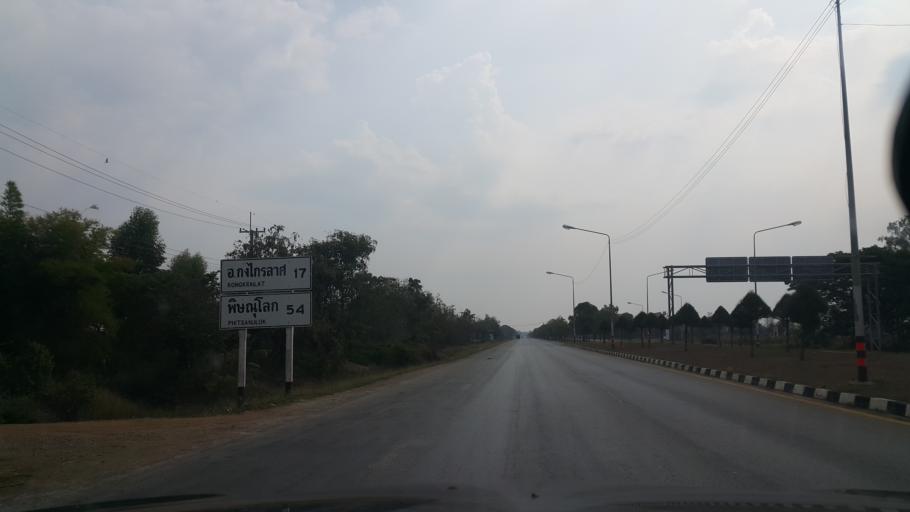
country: TH
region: Sukhothai
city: Sukhothai
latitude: 17.0638
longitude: 99.8780
